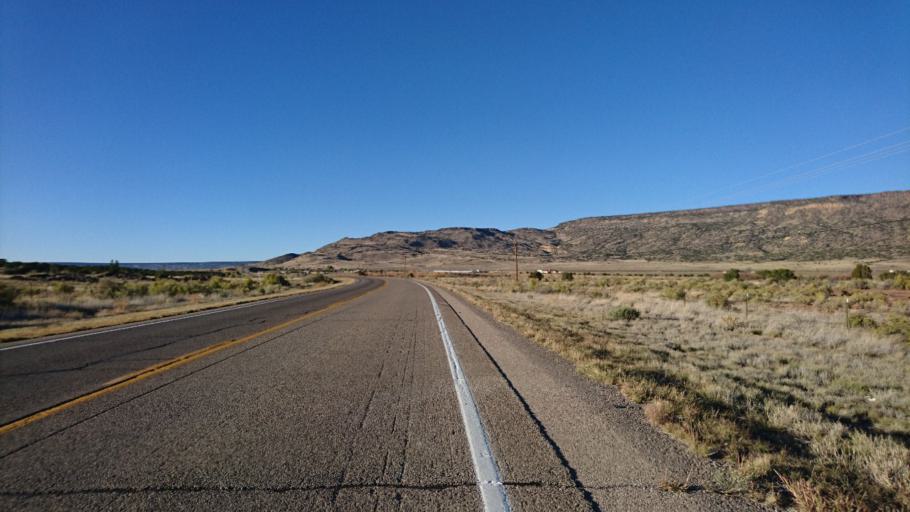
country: US
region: New Mexico
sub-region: Cibola County
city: Grants
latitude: 35.0940
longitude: -107.7716
